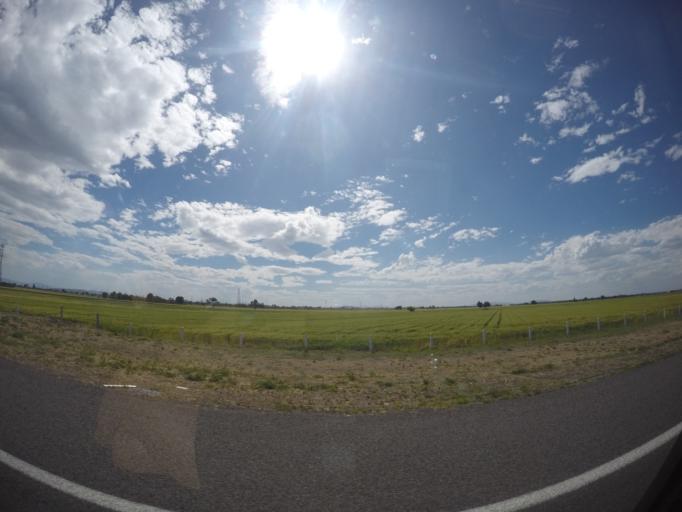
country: MX
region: Guanajuato
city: Cerro Gordo
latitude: 20.6128
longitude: -101.1454
